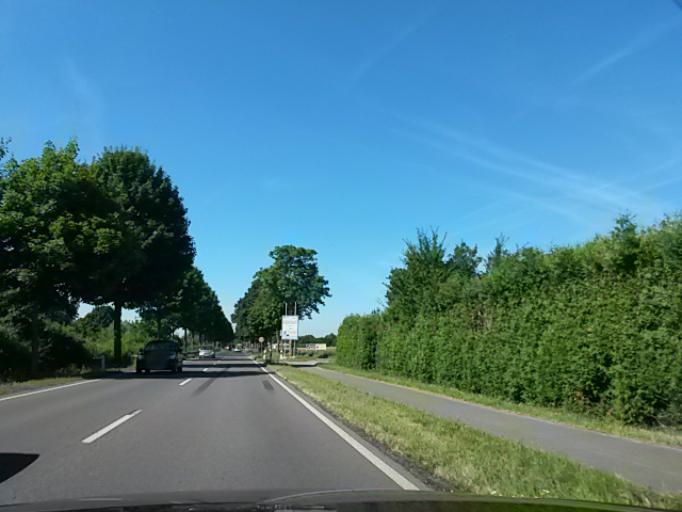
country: DE
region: North Rhine-Westphalia
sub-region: Regierungsbezirk Dusseldorf
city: Nettetal
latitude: 51.3139
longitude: 6.2984
